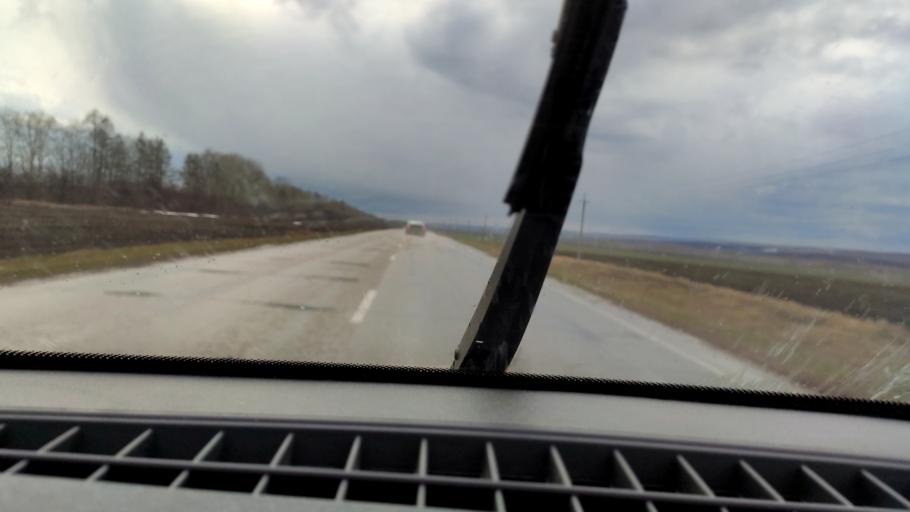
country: RU
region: Bashkortostan
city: Chekmagush
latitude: 55.1080
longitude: 54.9682
